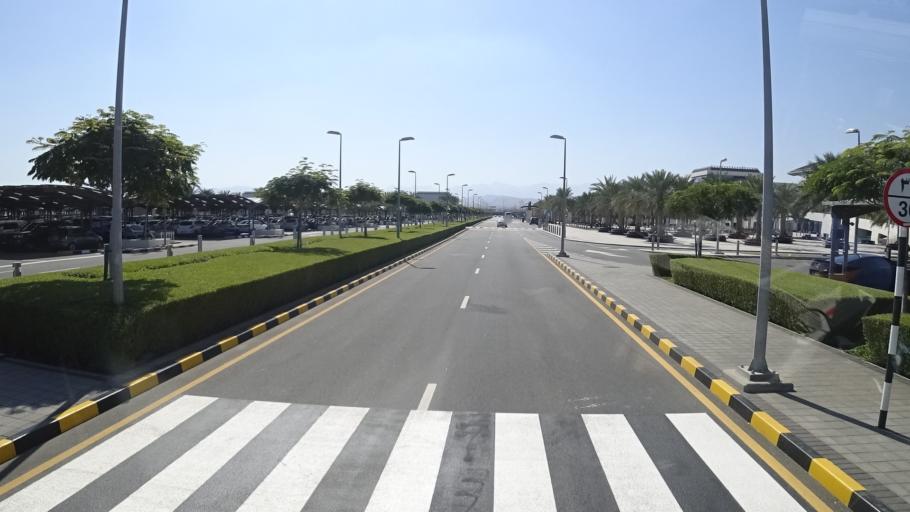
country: OM
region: Muhafazat Masqat
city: Bawshar
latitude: 23.6028
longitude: 58.2919
